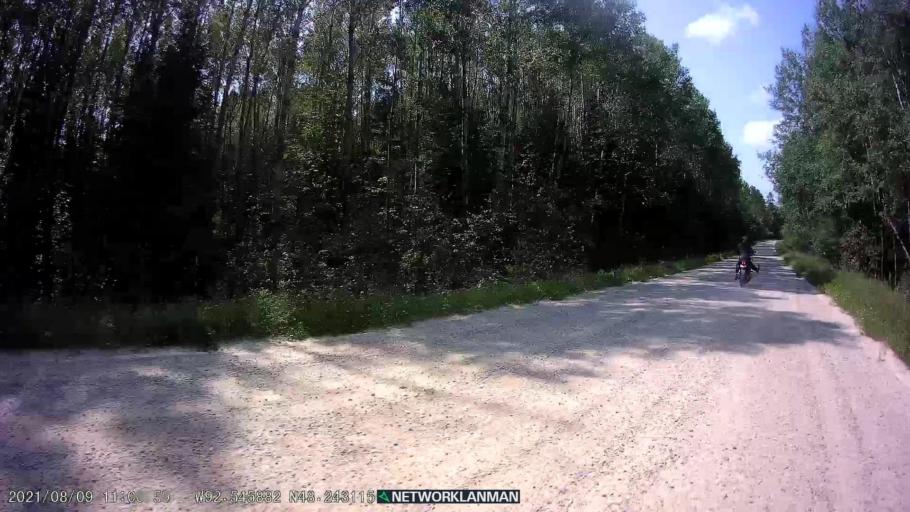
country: US
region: Minnesota
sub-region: Saint Louis County
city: Parkville
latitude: 48.2431
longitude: -92.5462
